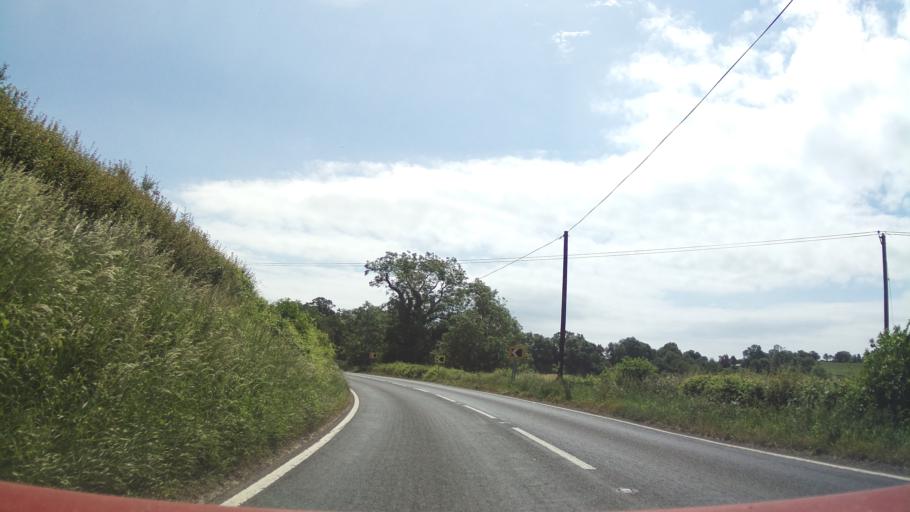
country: GB
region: England
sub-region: Somerset
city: Bruton
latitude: 51.0626
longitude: -2.4666
